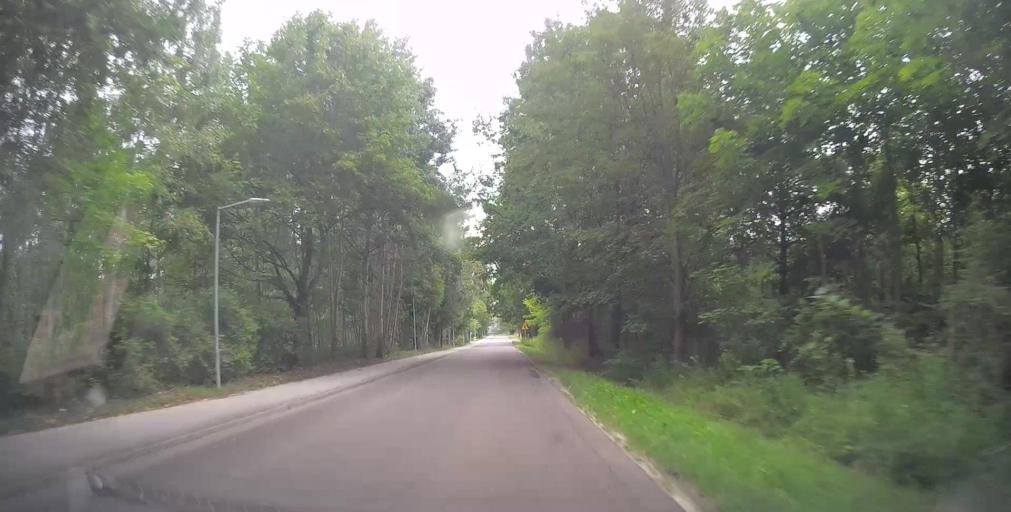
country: PL
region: Masovian Voivodeship
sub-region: Powiat bialobrzeski
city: Bialobrzegi
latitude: 51.6374
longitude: 20.9539
